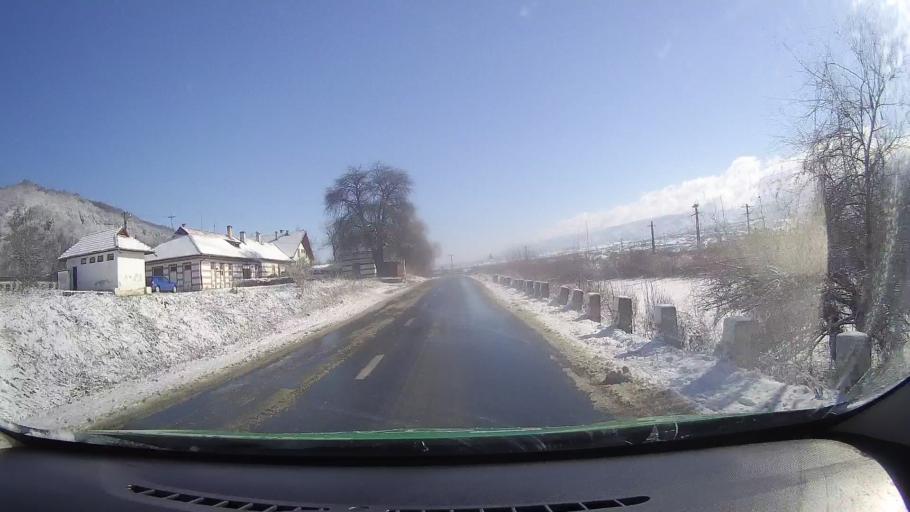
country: RO
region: Sibiu
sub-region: Comuna Turnu Rosu
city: Turnu Rosu
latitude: 45.6616
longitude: 24.2978
